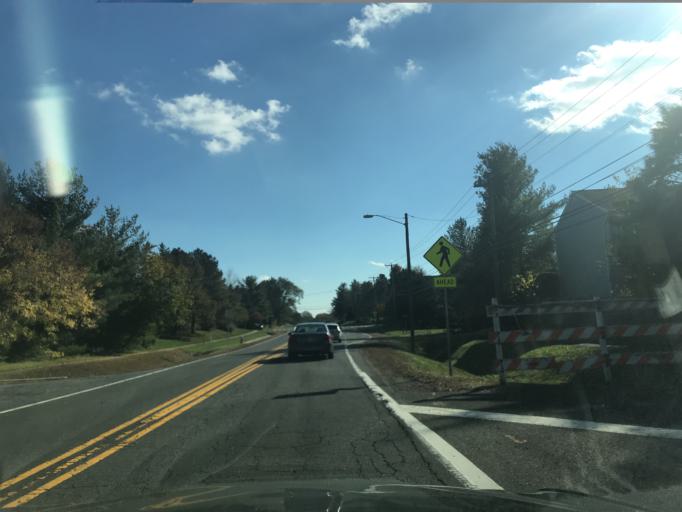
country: US
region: Virginia
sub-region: Fairfax County
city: Oak Hill
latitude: 38.9295
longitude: -77.4025
